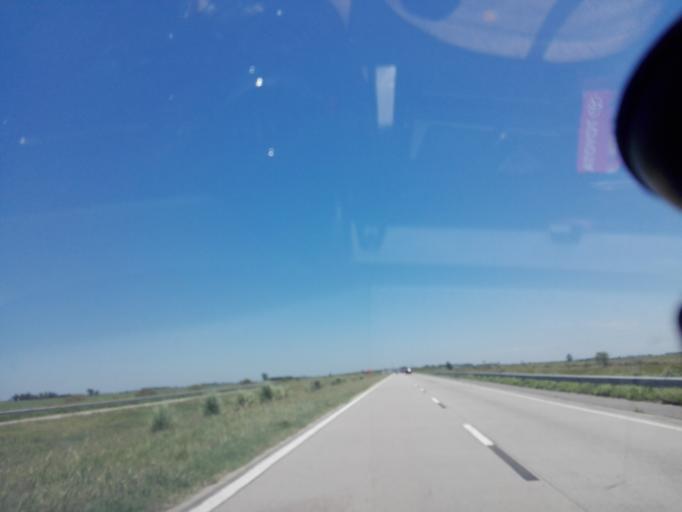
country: AR
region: Cordoba
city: Leones
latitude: -32.5992
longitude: -62.4620
